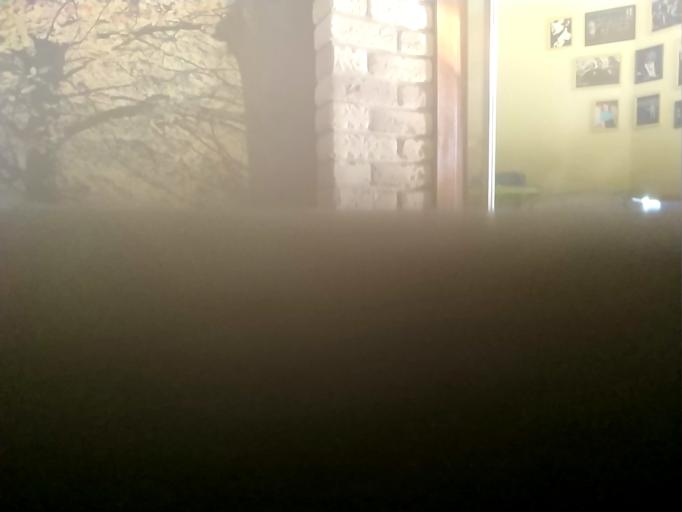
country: RU
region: Smolensk
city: Temkino
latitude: 54.8924
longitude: 34.9785
